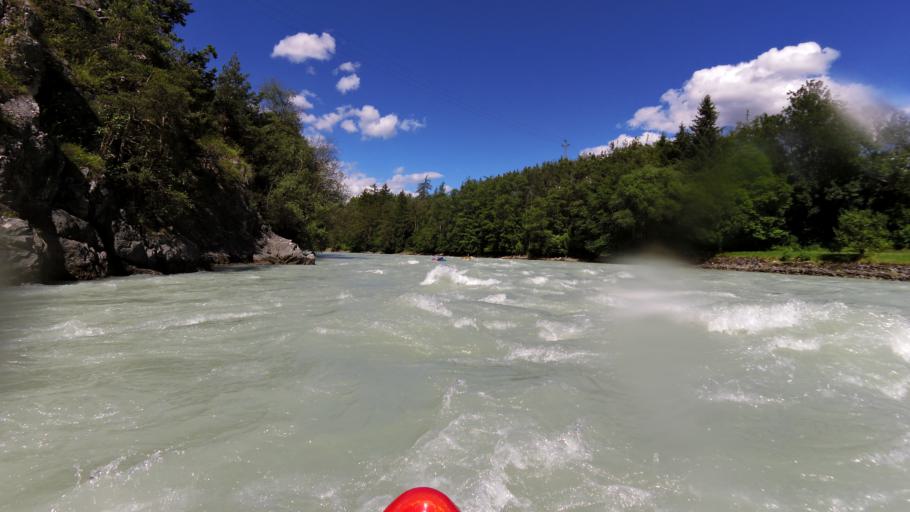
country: AT
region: Tyrol
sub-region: Politischer Bezirk Imst
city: Roppen
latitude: 47.2210
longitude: 10.8185
